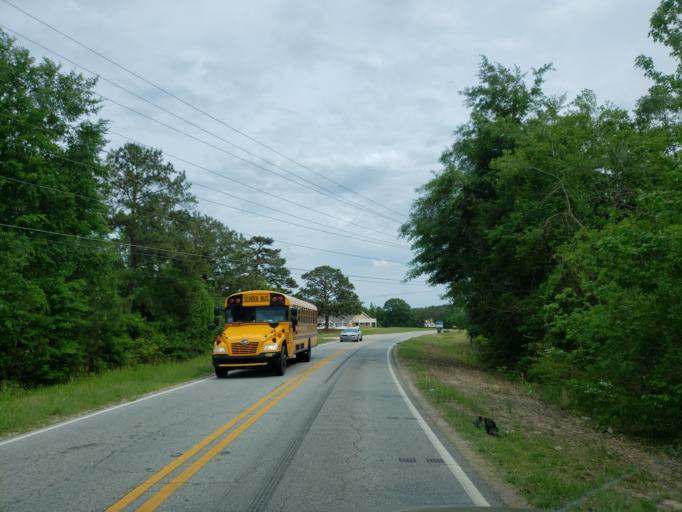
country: US
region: Georgia
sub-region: Bibb County
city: West Point
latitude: 32.7555
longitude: -83.7448
